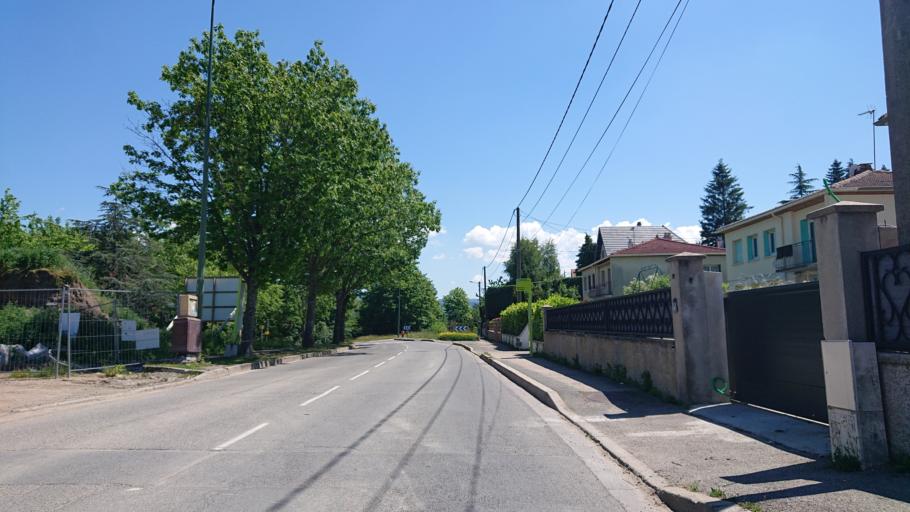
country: FR
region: Rhone-Alpes
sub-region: Departement de la Loire
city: Villars
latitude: 45.4515
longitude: 4.3597
